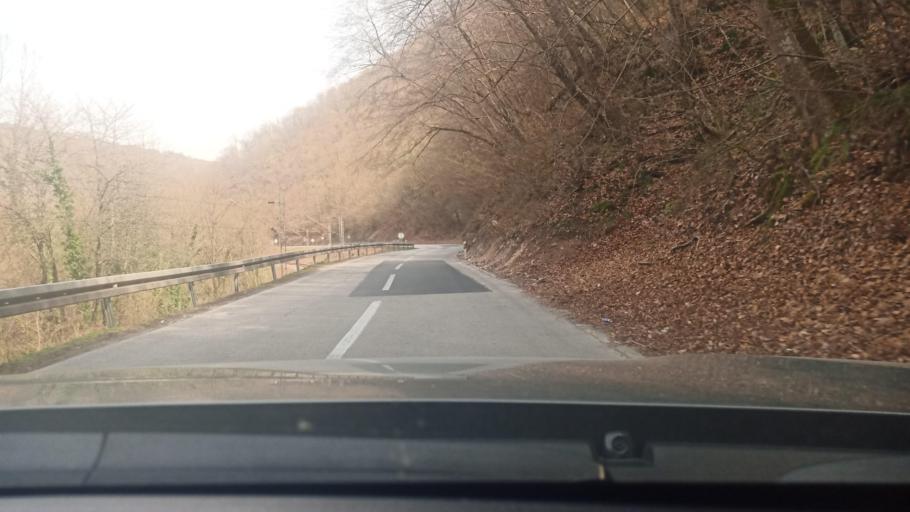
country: BA
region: Federation of Bosnia and Herzegovina
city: Ostrozac
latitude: 44.9055
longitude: 15.9584
